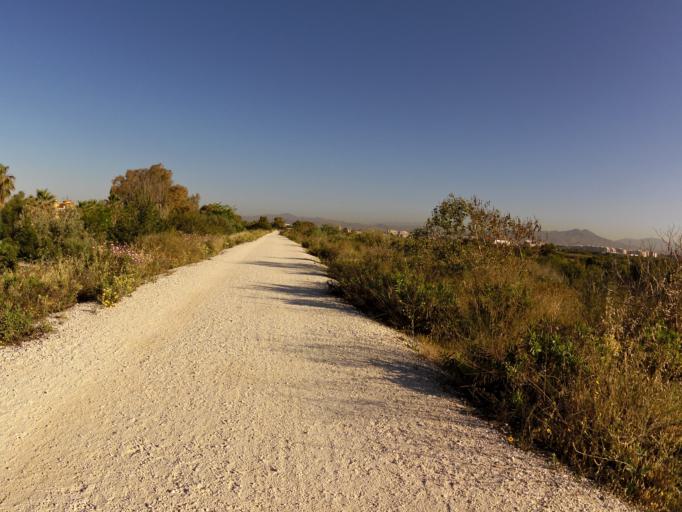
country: ES
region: Andalusia
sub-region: Provincia de Malaga
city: Torremolinos
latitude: 36.6669
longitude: -4.4571
